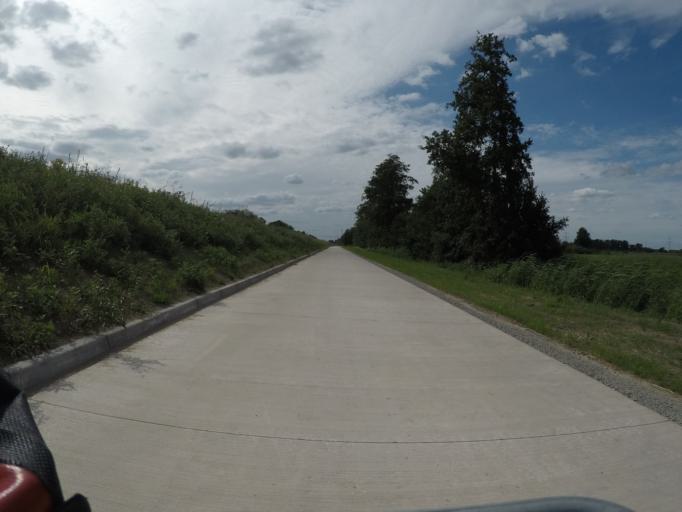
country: DE
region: Lower Saxony
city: Handorf
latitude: 53.3553
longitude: 10.3585
